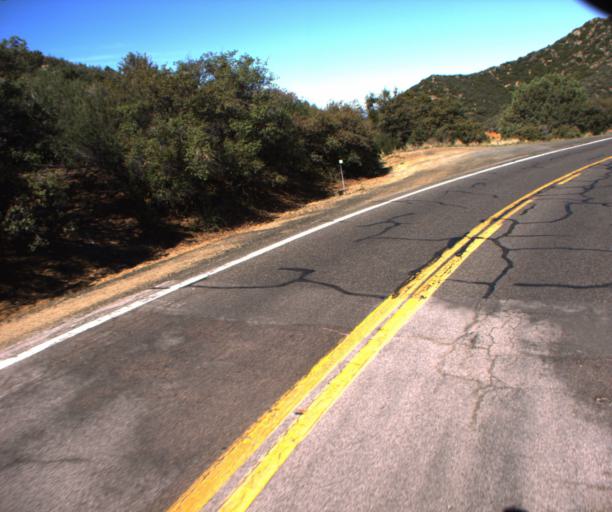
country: US
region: Arizona
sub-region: Yavapai County
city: Prescott
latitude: 34.4277
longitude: -112.5488
